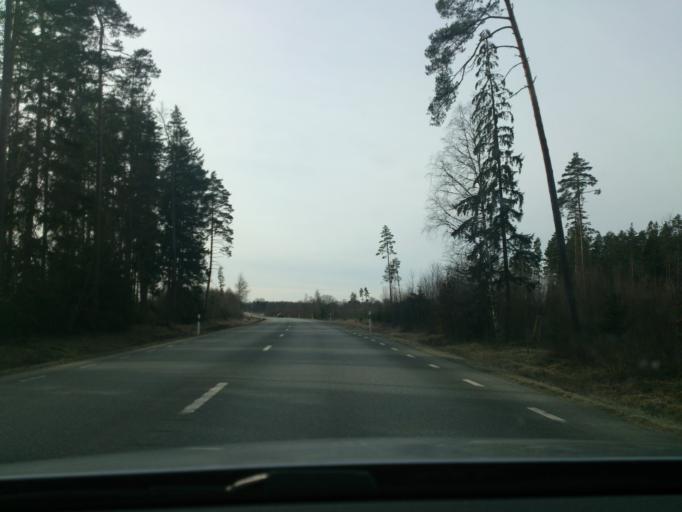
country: SE
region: Kronoberg
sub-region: Alvesta Kommun
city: Alvesta
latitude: 56.9435
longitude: 14.5611
